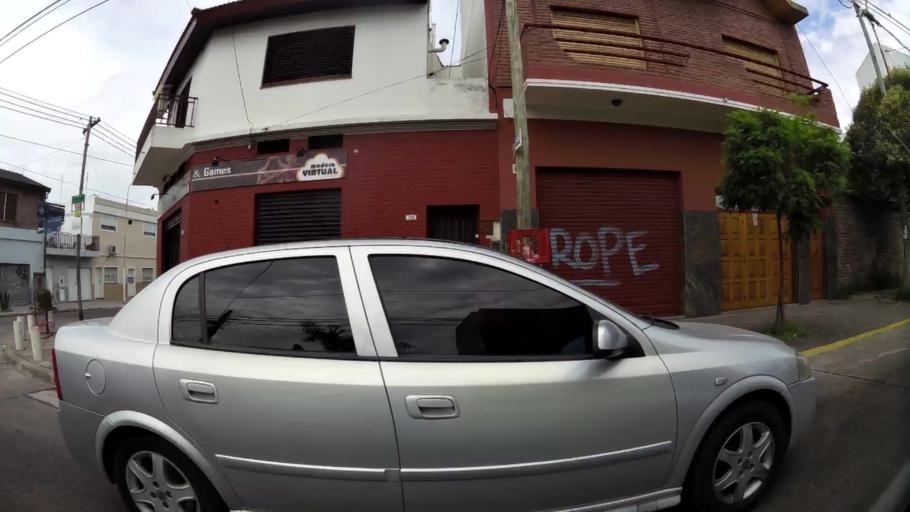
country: AR
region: Buenos Aires F.D.
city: Villa Lugano
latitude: -34.6845
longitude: -58.4981
